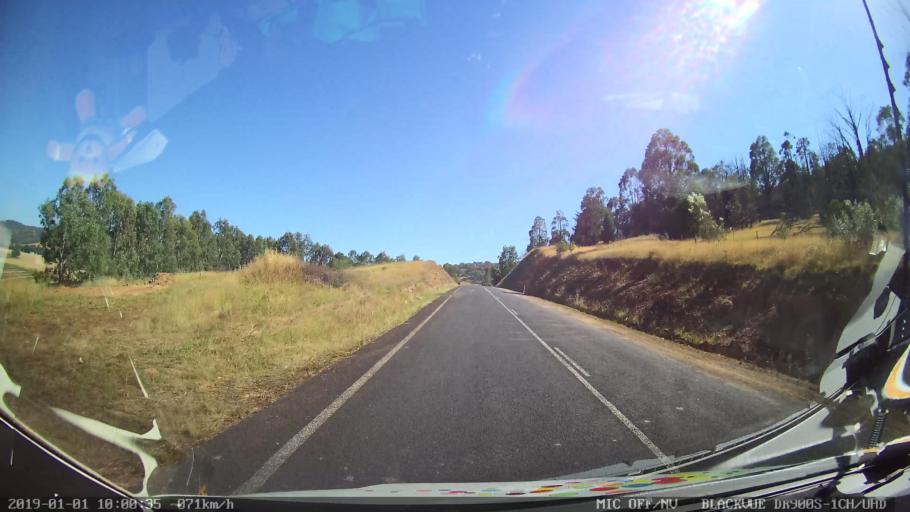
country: AU
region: New South Wales
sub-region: Snowy River
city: Jindabyne
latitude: -36.2006
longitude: 148.1021
